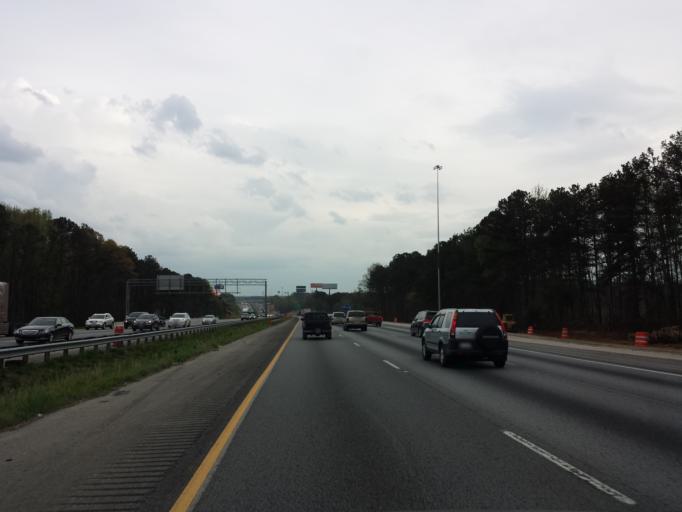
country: US
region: Georgia
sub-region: Henry County
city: Stockbridge
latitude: 33.4785
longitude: -84.2163
